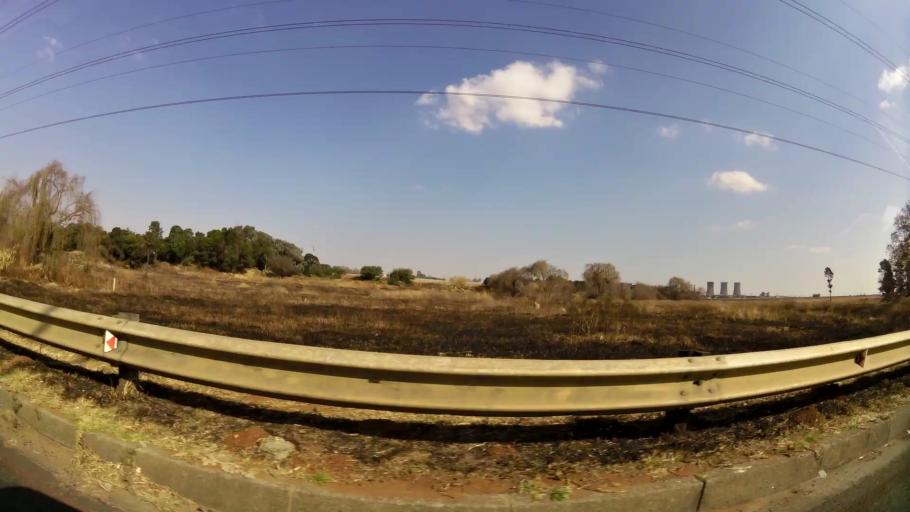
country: ZA
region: Gauteng
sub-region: City of Johannesburg Metropolitan Municipality
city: Modderfontein
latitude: -26.0994
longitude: 28.2111
